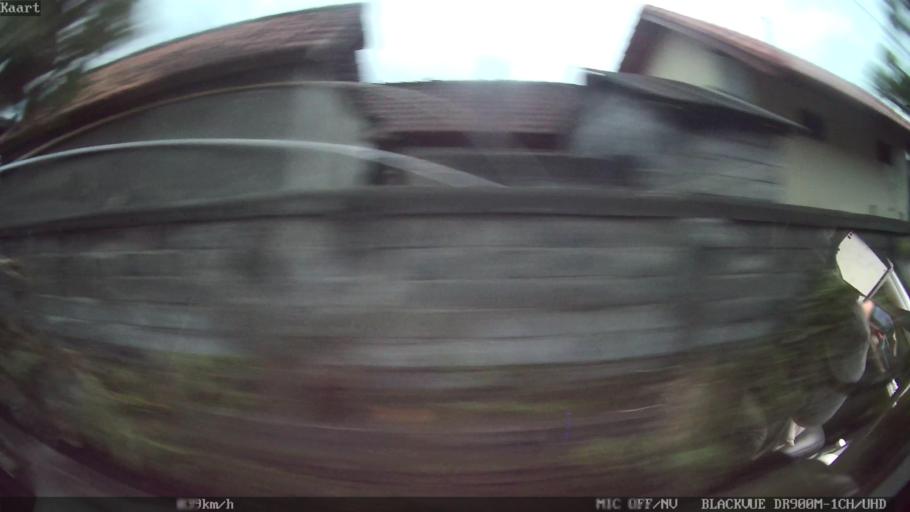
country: ID
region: Bali
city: Banjar Pasekan
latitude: -8.6254
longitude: 115.2811
